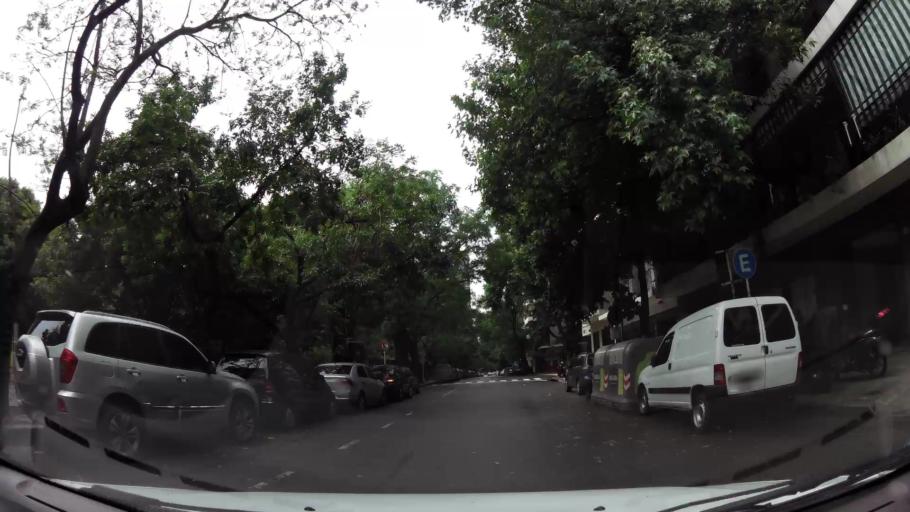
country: AR
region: Buenos Aires F.D.
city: Retiro
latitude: -34.5836
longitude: -58.4158
